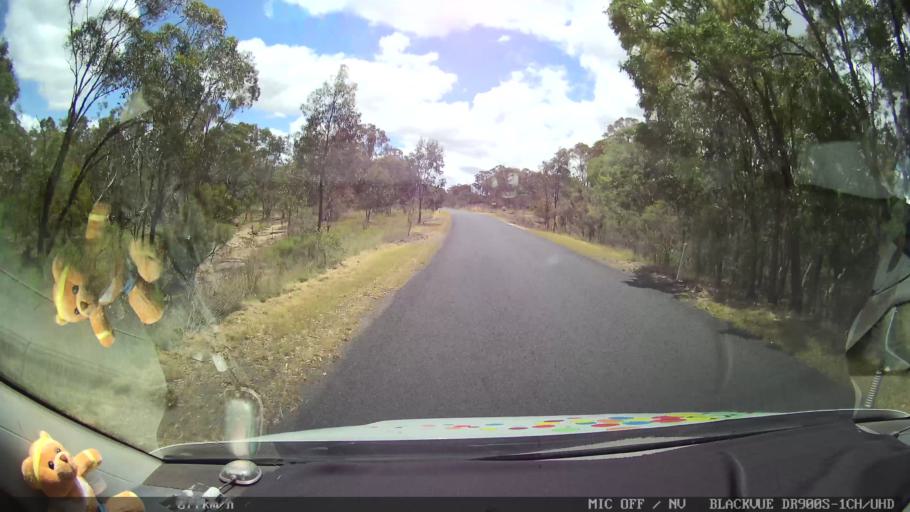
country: AU
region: New South Wales
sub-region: Glen Innes Severn
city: Glen Innes
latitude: -29.4312
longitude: 151.7905
